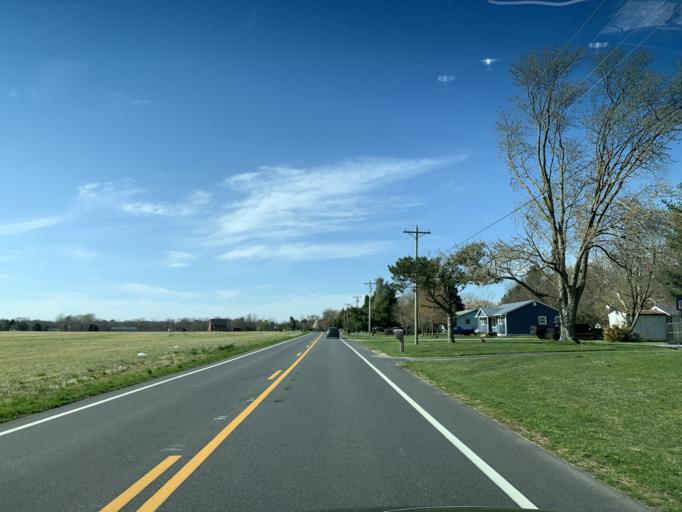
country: US
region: Delaware
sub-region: Kent County
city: Riverview
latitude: 39.0302
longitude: -75.5450
